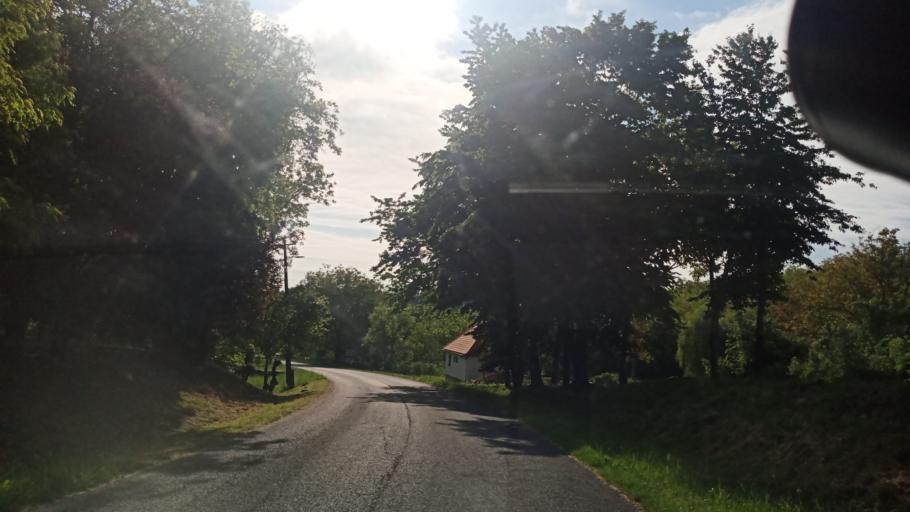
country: HU
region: Zala
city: Pacsa
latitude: 46.7030
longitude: 17.0563
